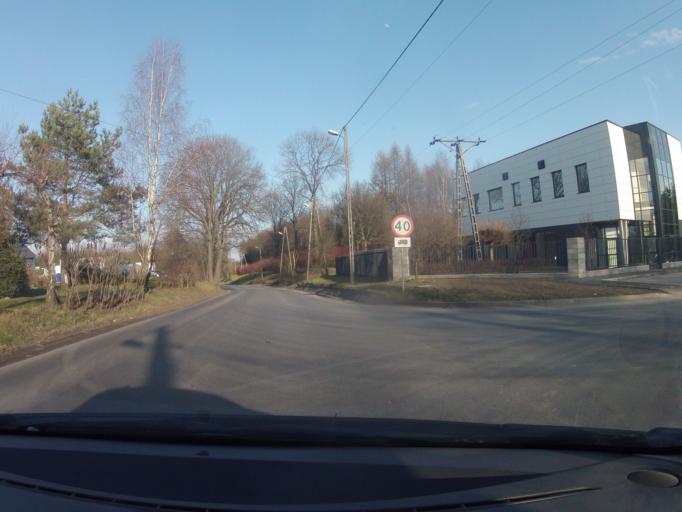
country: PL
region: Lesser Poland Voivodeship
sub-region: Powiat krakowski
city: Ochojno
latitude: 49.9851
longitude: 20.0036
